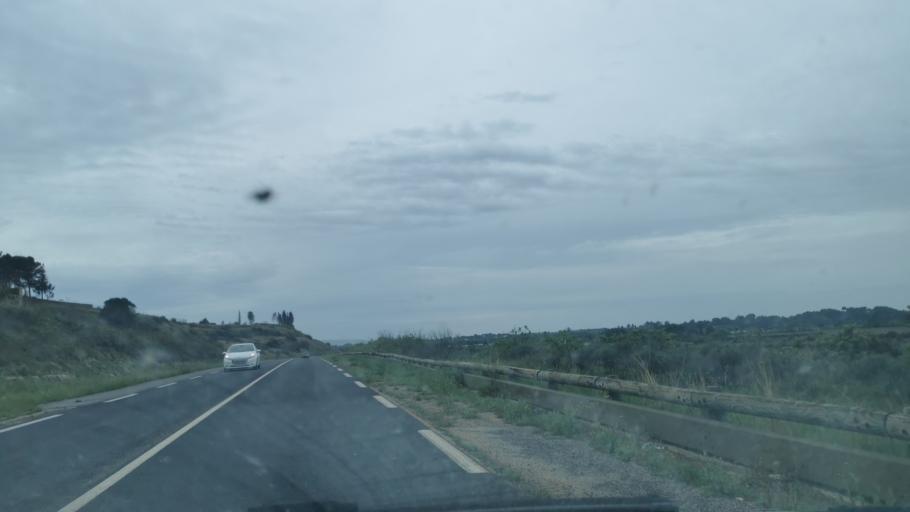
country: FR
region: Languedoc-Roussillon
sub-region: Departement de l'Herault
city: Montbazin
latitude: 43.5066
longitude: 3.6840
